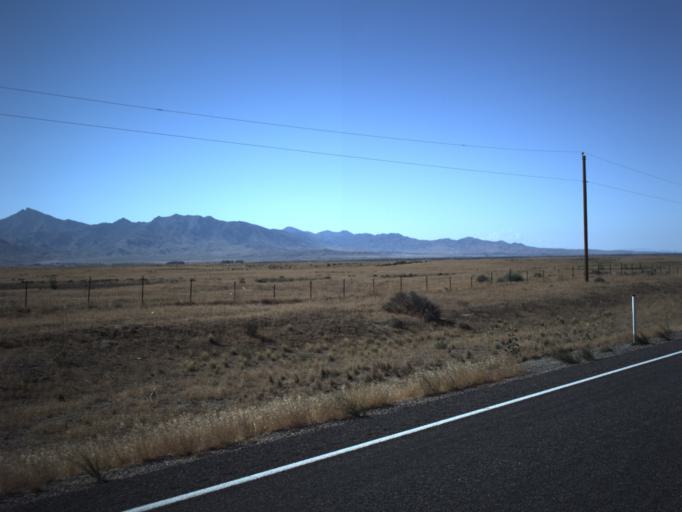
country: US
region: Utah
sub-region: Millard County
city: Delta
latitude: 39.5763
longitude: -112.3397
